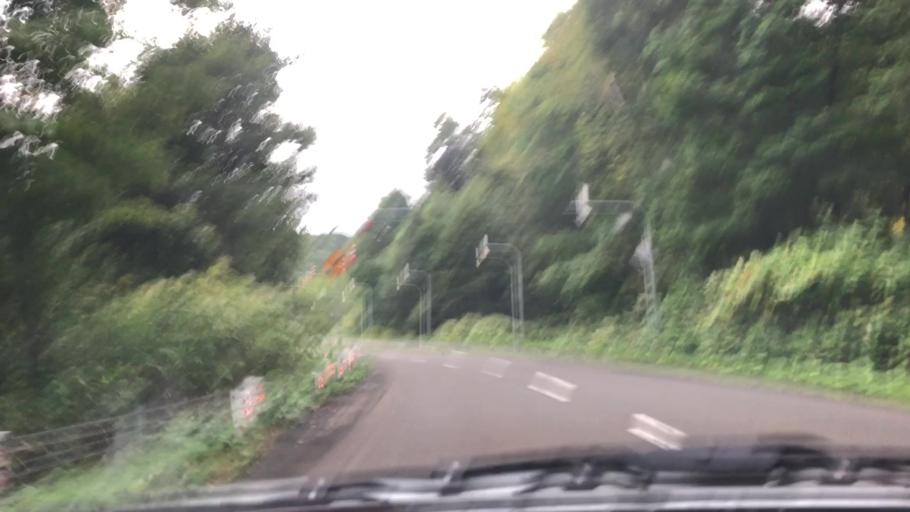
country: JP
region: Hokkaido
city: Shimo-furano
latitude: 42.9274
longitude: 142.3731
